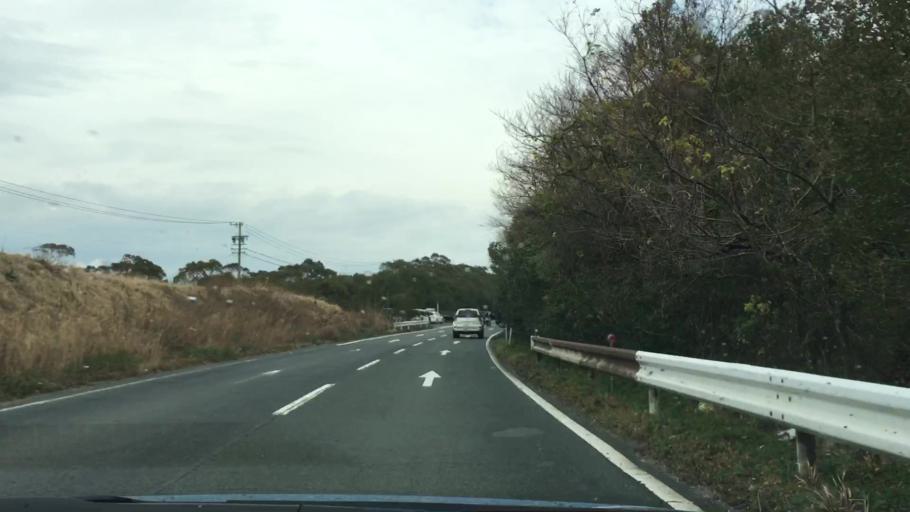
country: JP
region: Aichi
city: Tahara
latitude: 34.6994
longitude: 137.3257
